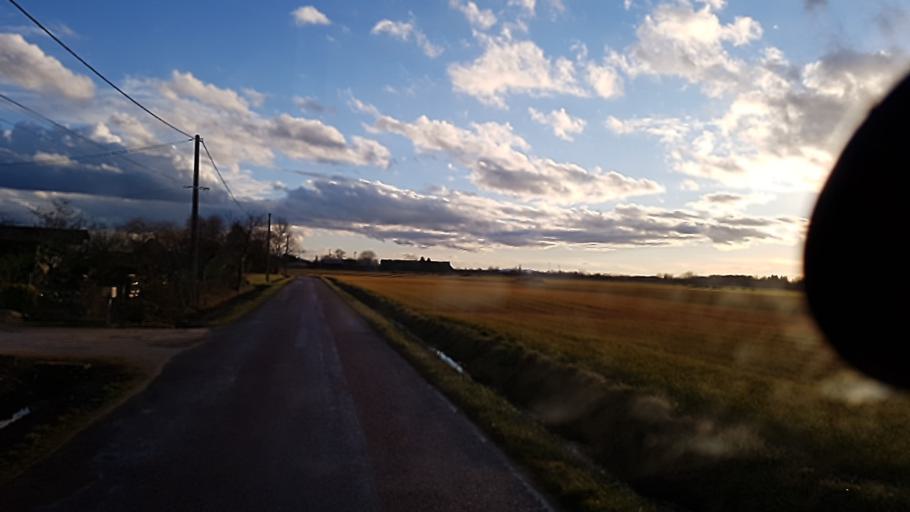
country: FR
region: Bourgogne
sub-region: Departement de Saone-et-Loire
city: Saint-Martin-en-Bresse
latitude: 46.7632
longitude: 5.1063
